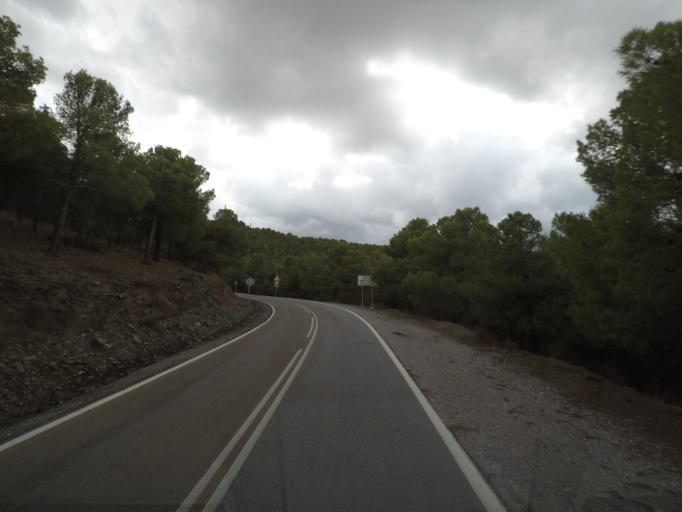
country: ES
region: Andalusia
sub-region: Provincia de Granada
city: Ferreira
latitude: 37.1727
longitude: -3.0490
